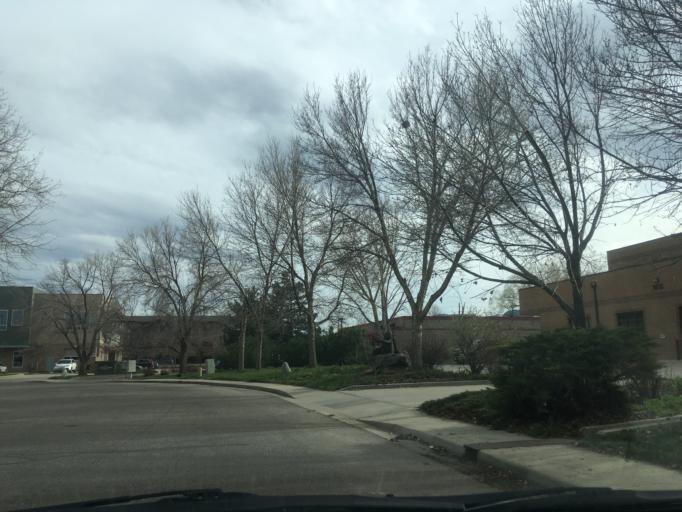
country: US
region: Colorado
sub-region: Boulder County
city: Boulder
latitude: 40.0305
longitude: -105.2282
